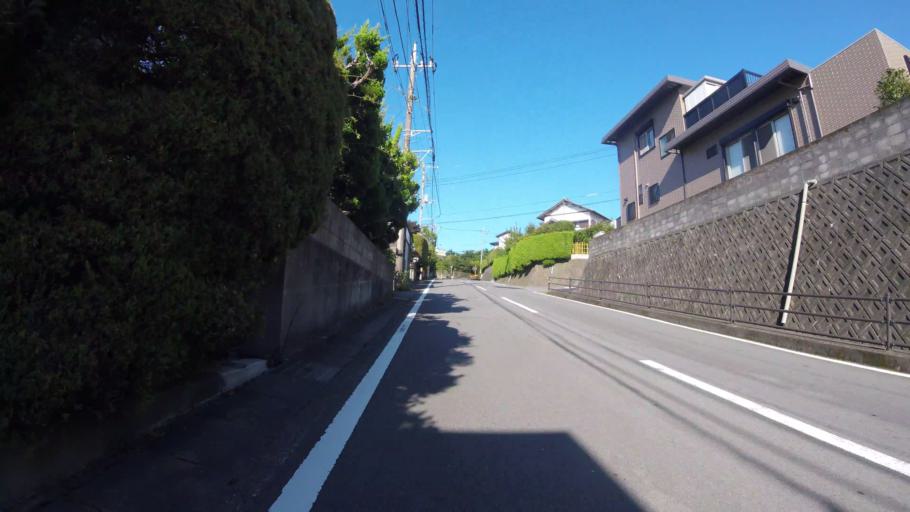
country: JP
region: Shizuoka
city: Mishima
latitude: 35.1374
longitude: 138.9250
